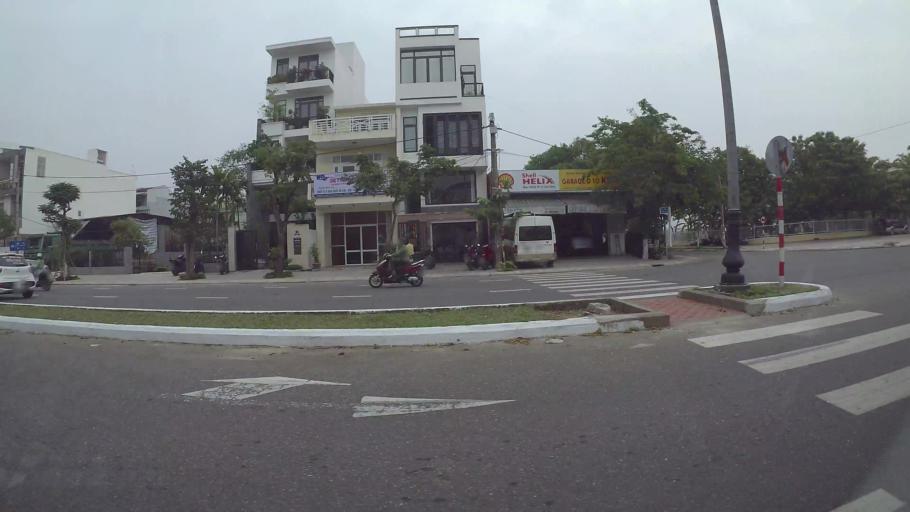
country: VN
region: Da Nang
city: Cam Le
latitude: 16.0291
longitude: 108.2128
